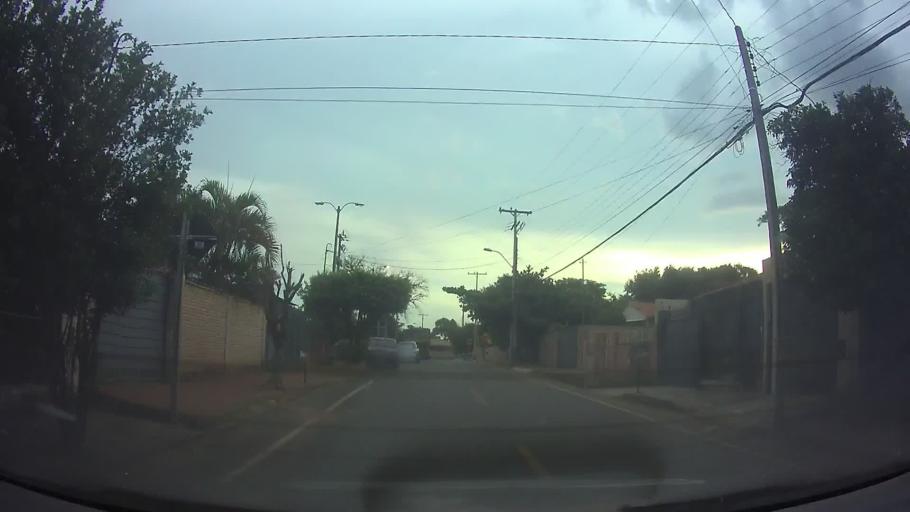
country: PY
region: Central
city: San Lorenzo
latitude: -25.2730
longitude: -57.4662
